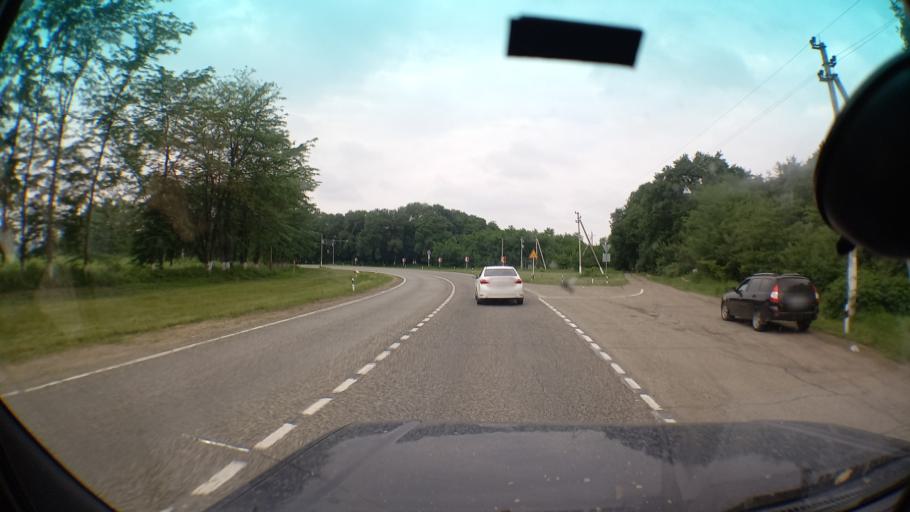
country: RU
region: Krasnodarskiy
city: Mostovskoy
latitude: 44.4496
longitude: 40.7713
